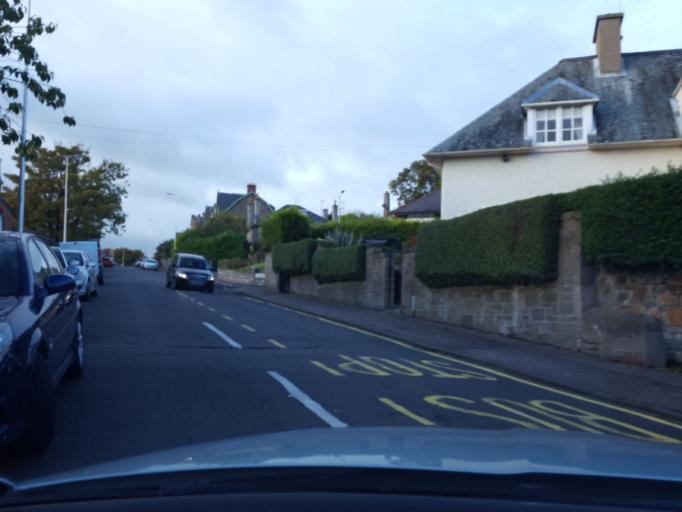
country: GB
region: Scotland
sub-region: Dundee City
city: Dundee
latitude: 56.4666
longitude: -2.9927
